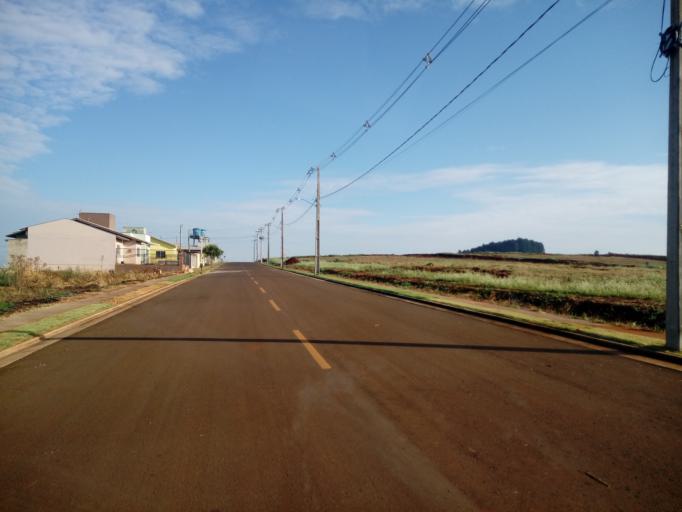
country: BR
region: Santa Catarina
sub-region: Chapeco
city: Chapeco
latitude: -27.0895
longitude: -52.7091
